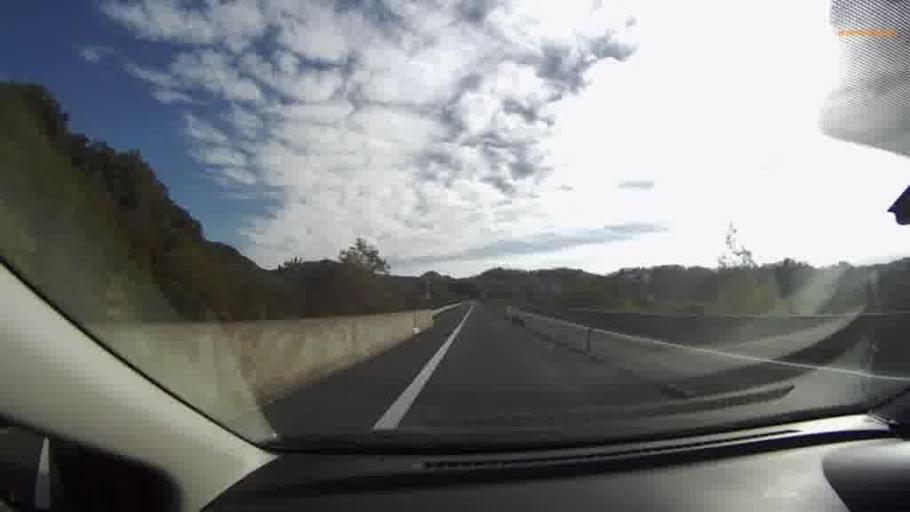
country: JP
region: Hokkaido
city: Kushiro
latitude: 43.0796
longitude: 143.9694
